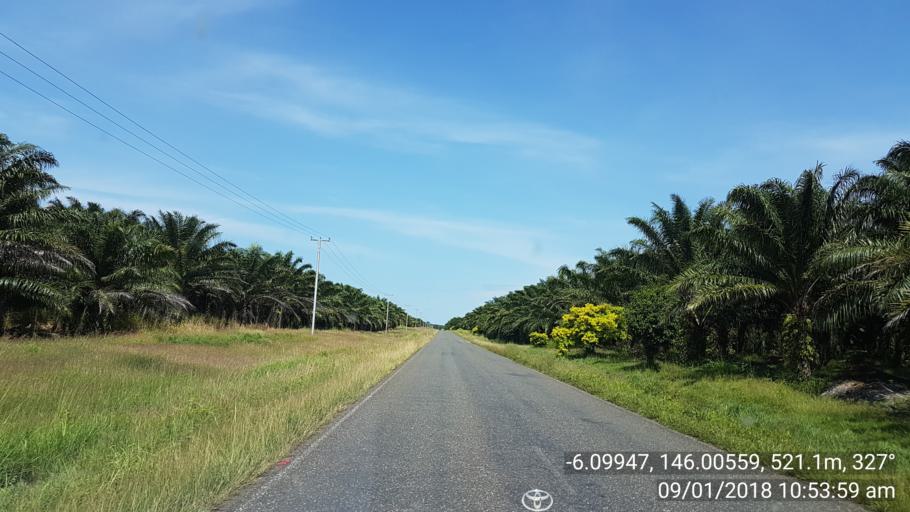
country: PG
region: Eastern Highlands
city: Kainantu
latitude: -6.0997
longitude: 146.0058
